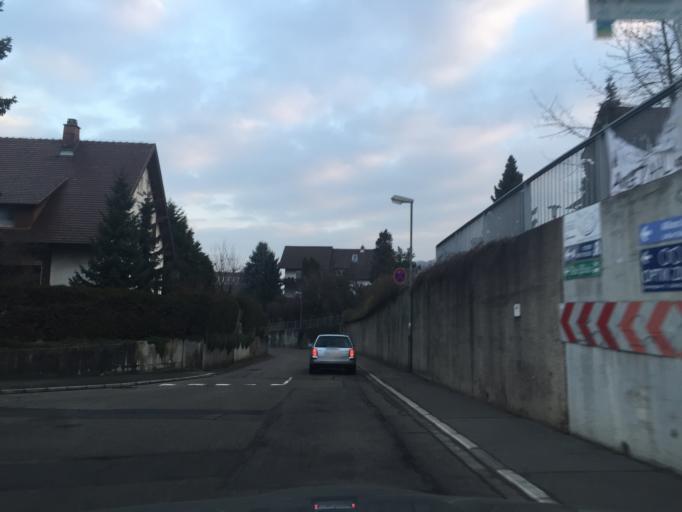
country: DE
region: Baden-Wuerttemberg
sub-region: Karlsruhe Region
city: Weinheim
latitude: 49.5235
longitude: 8.6680
